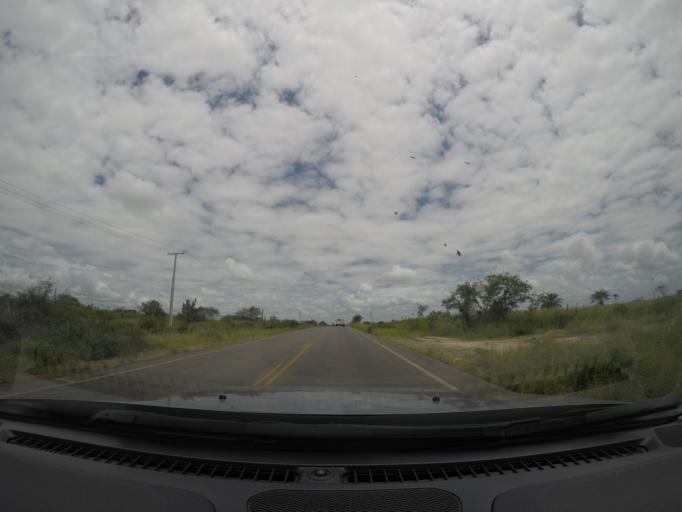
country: BR
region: Bahia
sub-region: Itaberaba
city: Itaberaba
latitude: -12.4783
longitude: -40.2042
